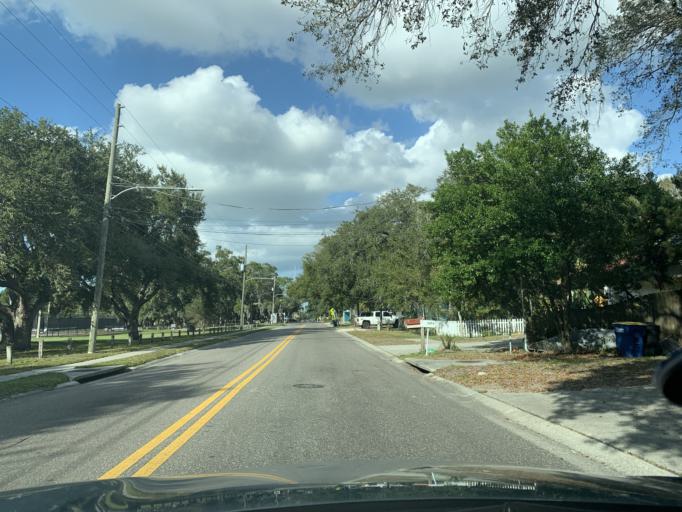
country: US
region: Florida
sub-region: Pinellas County
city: Belleair
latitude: 27.9470
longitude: -82.7916
